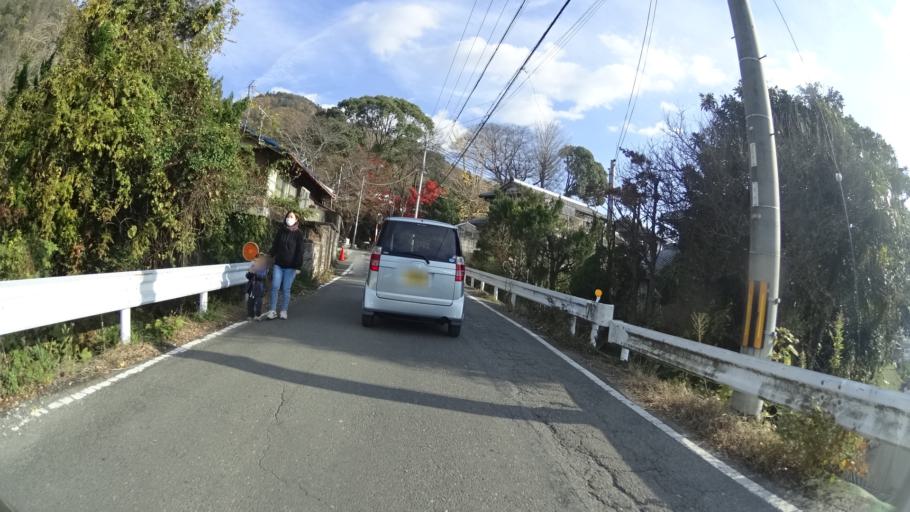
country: JP
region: Kyoto
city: Kameoka
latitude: 35.0583
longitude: 135.5779
